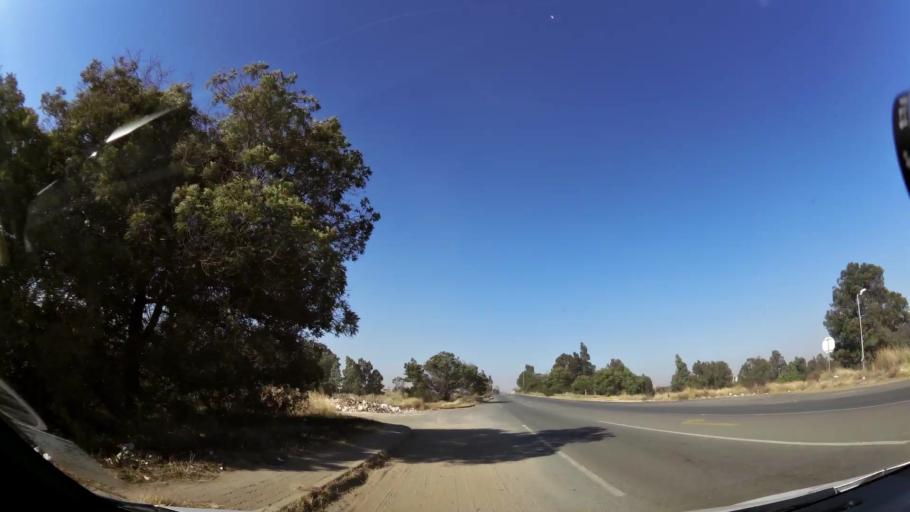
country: ZA
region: Gauteng
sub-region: Ekurhuleni Metropolitan Municipality
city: Germiston
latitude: -26.2189
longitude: 28.1148
